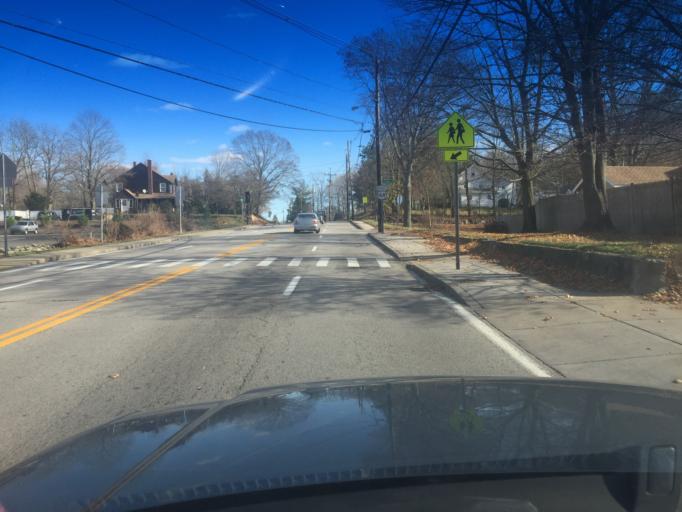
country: US
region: Rhode Island
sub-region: Providence County
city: Greenville
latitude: 41.8707
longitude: -71.5490
